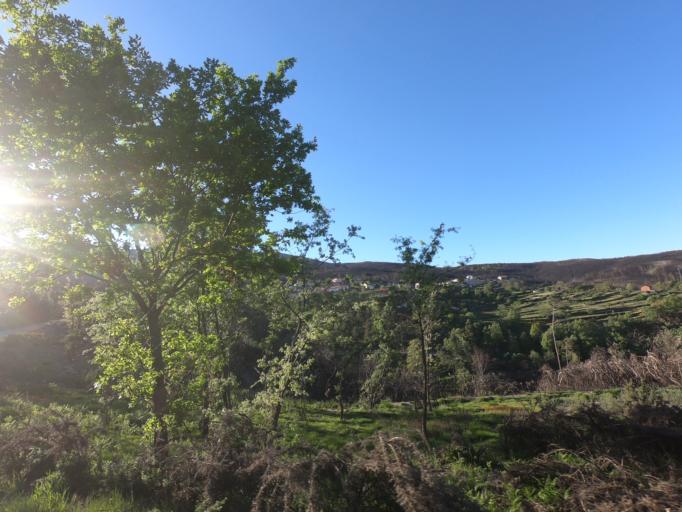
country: PT
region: Vila Real
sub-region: Vila Real
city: Vila Real
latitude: 41.3464
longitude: -7.7455
